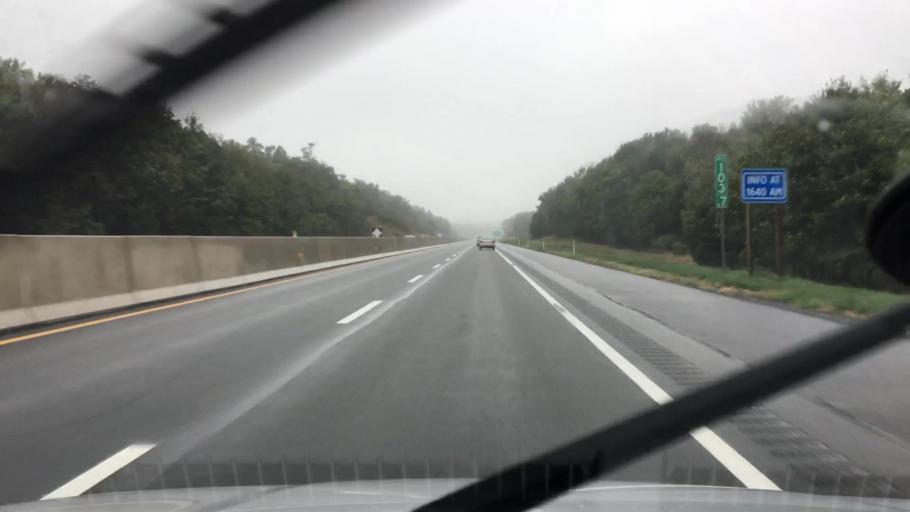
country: US
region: Pennsylvania
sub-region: Luzerne County
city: Mountain Top
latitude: 41.1768
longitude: -75.7824
